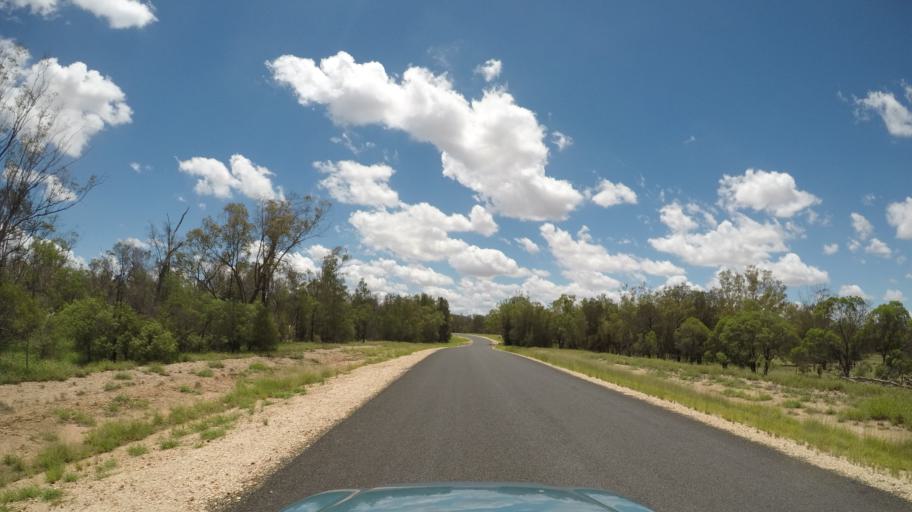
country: AU
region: Queensland
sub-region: Goondiwindi
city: Goondiwindi
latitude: -28.1508
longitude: 150.1264
